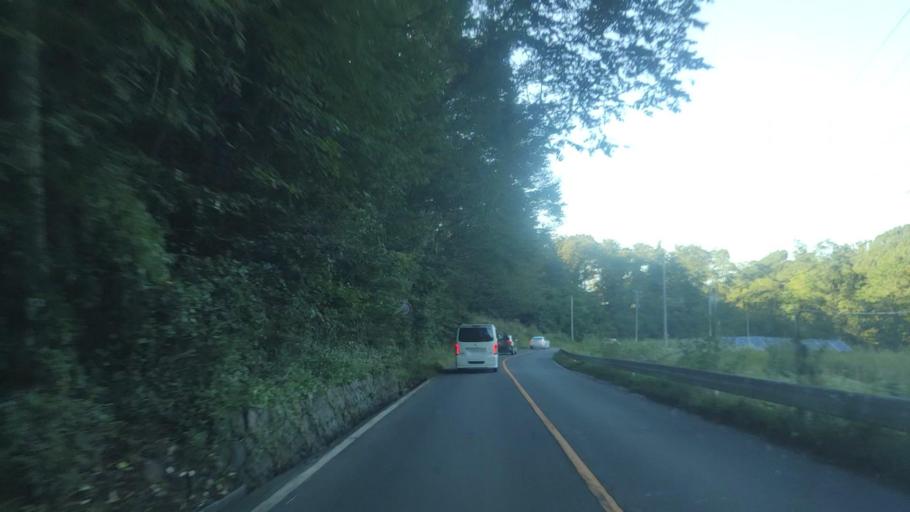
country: JP
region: Nagano
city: Kamimaruko
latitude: 36.2493
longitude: 138.3119
